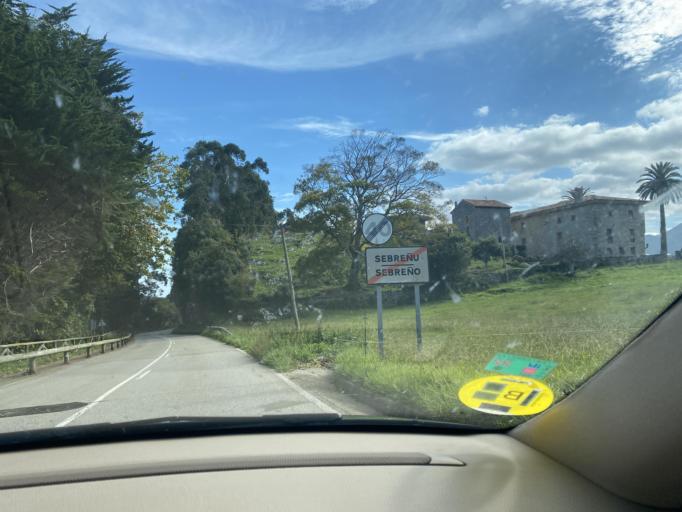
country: ES
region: Asturias
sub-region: Province of Asturias
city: Ribadesella
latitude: 43.4633
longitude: -5.0841
